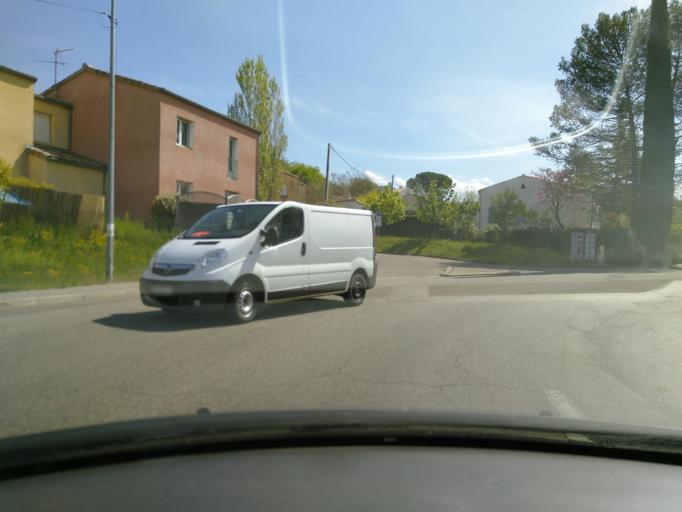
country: FR
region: Rhone-Alpes
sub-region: Departement de l'Ardeche
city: Ruoms
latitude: 44.4501
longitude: 4.3484
